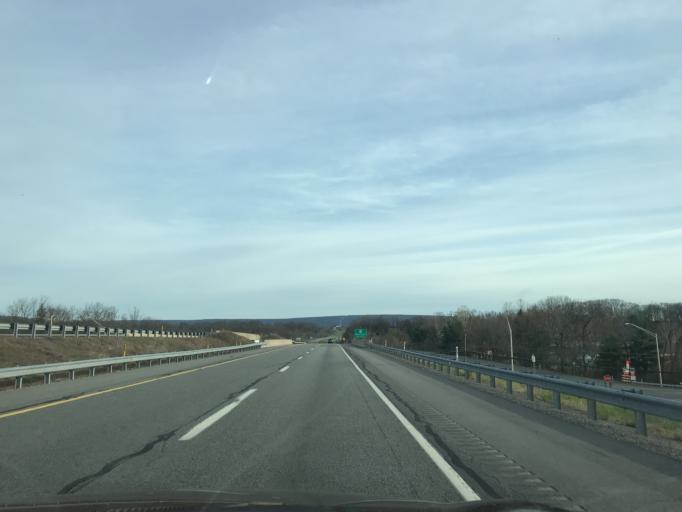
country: US
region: Pennsylvania
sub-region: Northumberland County
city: Milton
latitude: 41.0222
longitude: -76.8345
